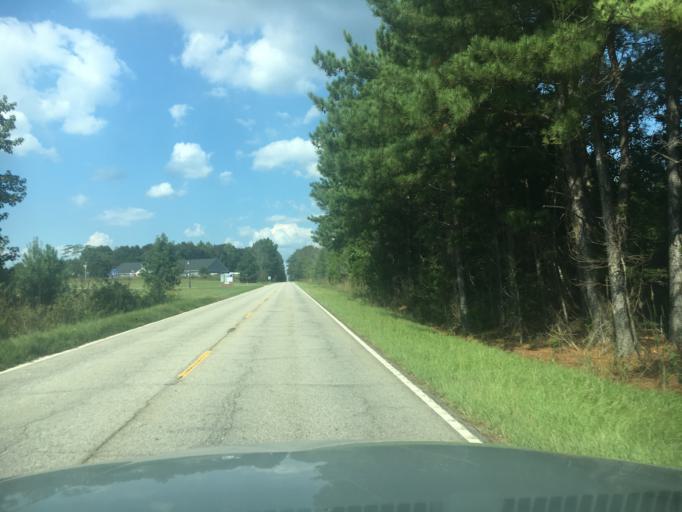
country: US
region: South Carolina
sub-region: Anderson County
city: Pendleton
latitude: 34.6863
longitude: -82.7490
